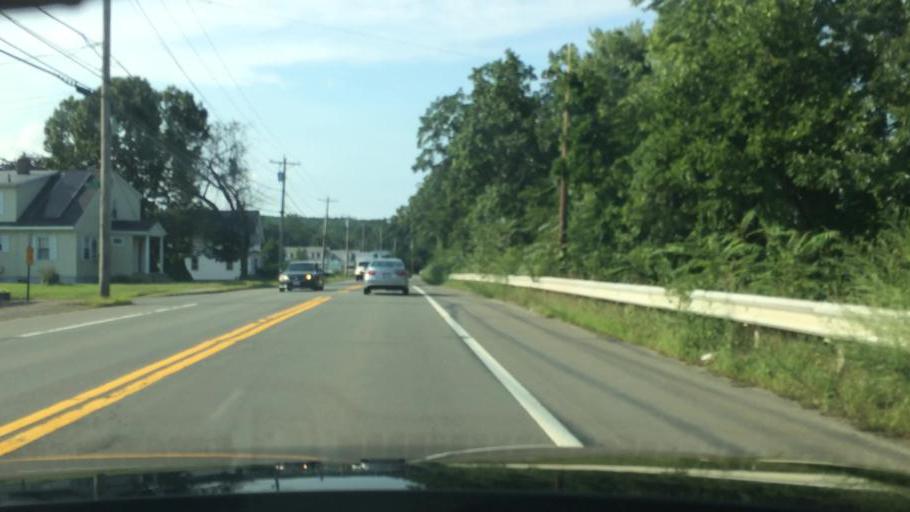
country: US
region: Massachusetts
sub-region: Essex County
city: Haverhill
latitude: 42.7572
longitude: -71.1311
